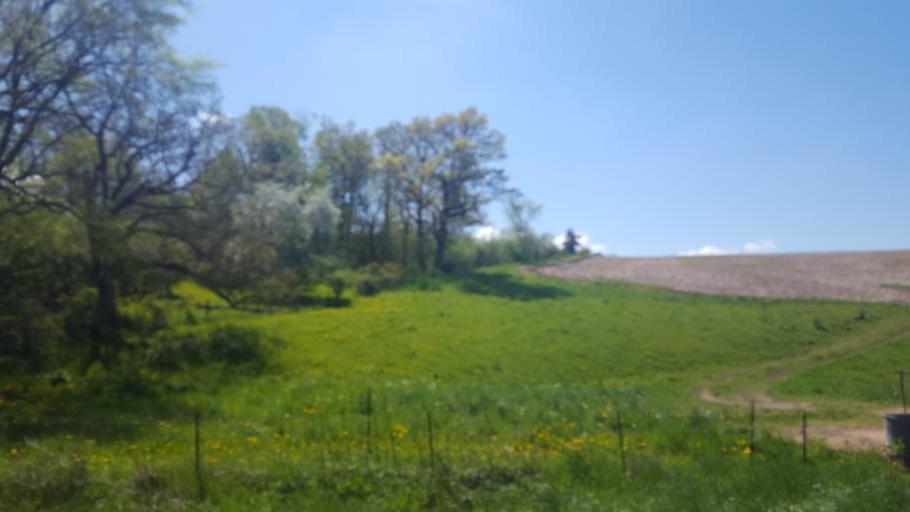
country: US
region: Wisconsin
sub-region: Vernon County
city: Hillsboro
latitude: 43.5785
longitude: -90.3669
